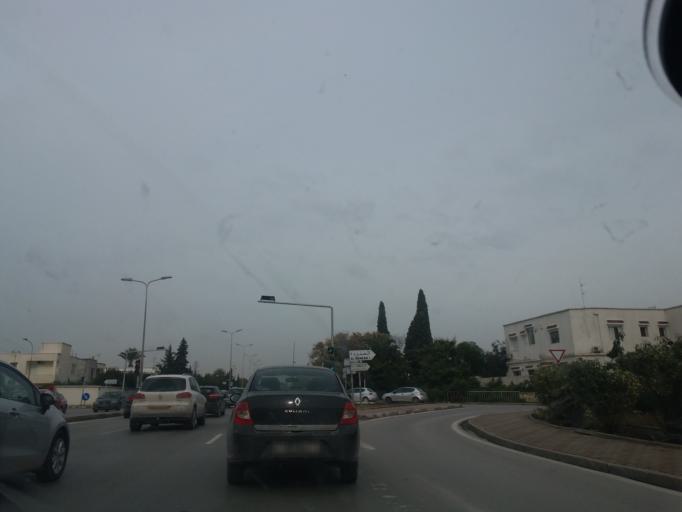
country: TN
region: Tunis
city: Tunis
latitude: 36.8362
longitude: 10.1745
